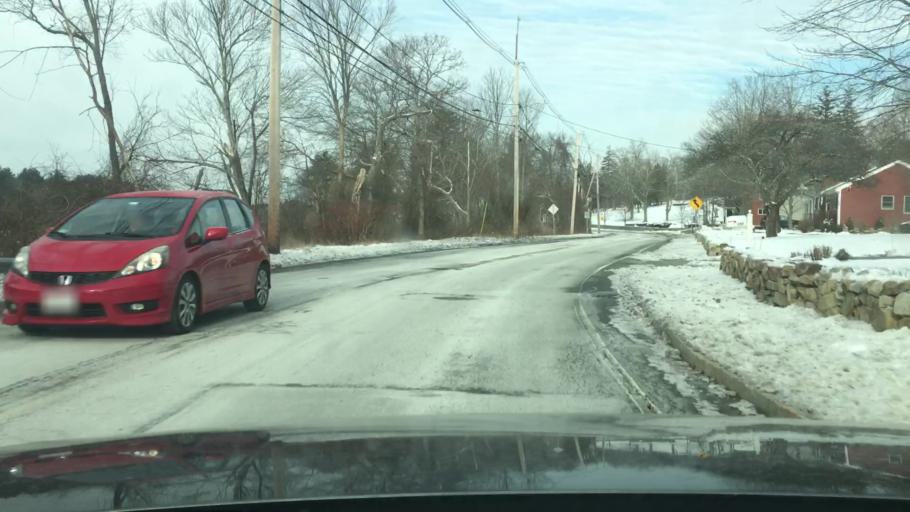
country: US
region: Massachusetts
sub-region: Middlesex County
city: North Reading
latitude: 42.5739
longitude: -71.0541
